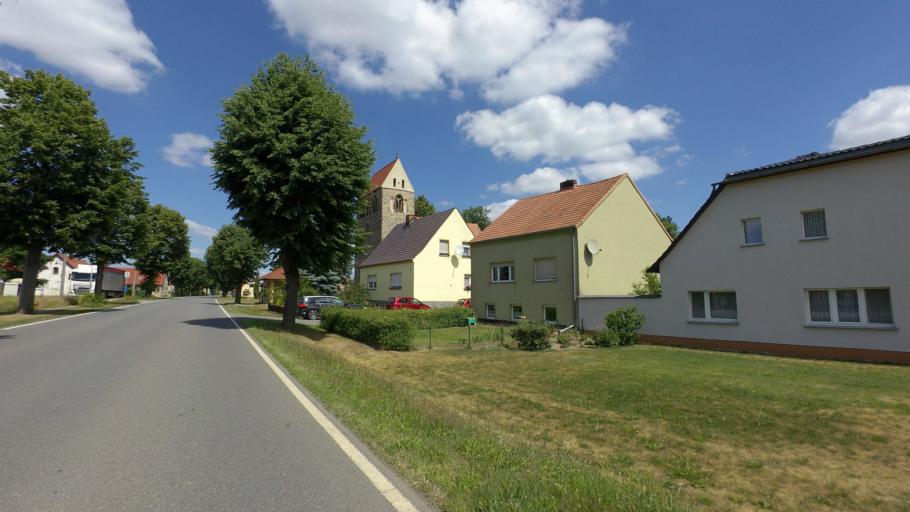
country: DE
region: Brandenburg
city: Luckau
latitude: 51.8041
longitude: 13.6788
